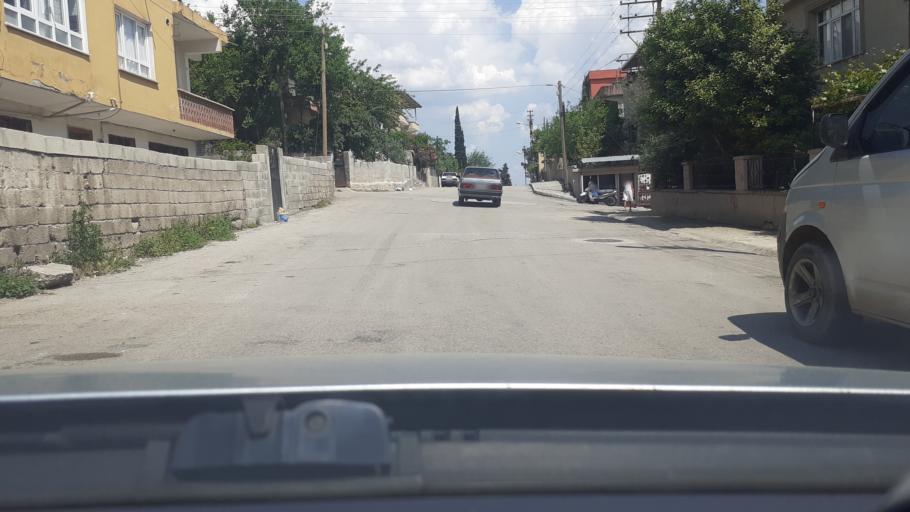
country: TR
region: Hatay
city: Kirikhan
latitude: 36.5023
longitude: 36.3554
